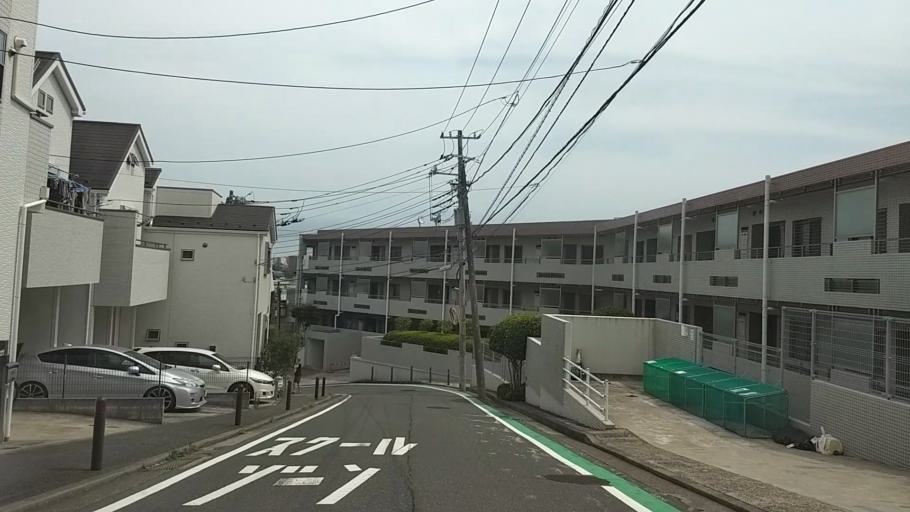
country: JP
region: Kanagawa
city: Yokohama
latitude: 35.4367
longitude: 139.6043
